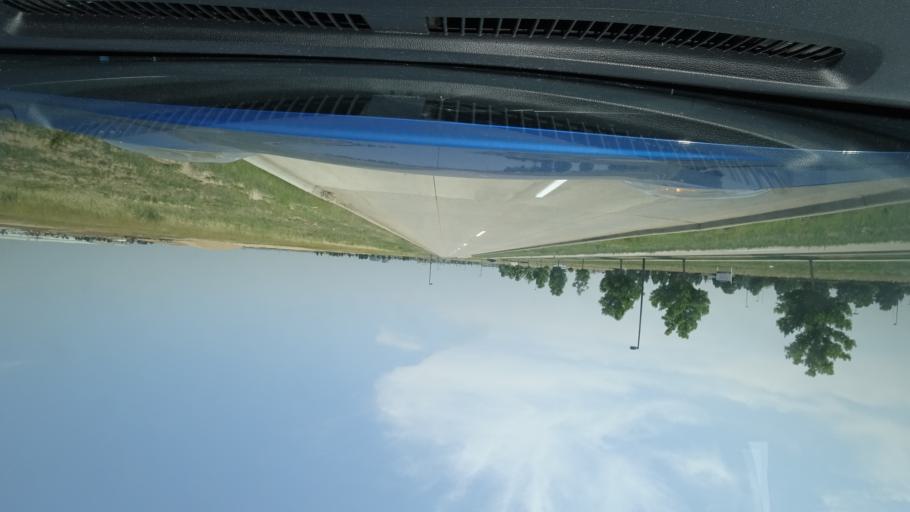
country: US
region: Colorado
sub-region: Adams County
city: Aurora
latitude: 39.7656
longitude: -104.7790
